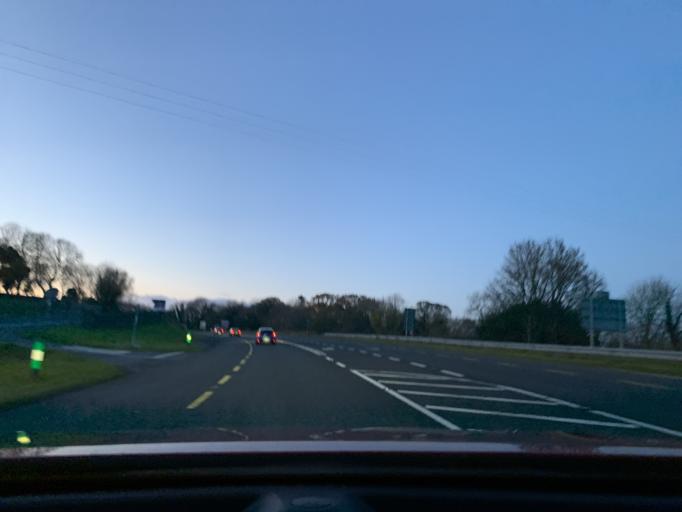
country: IE
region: Connaught
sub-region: Roscommon
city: Boyle
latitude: 53.9694
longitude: -8.2024
